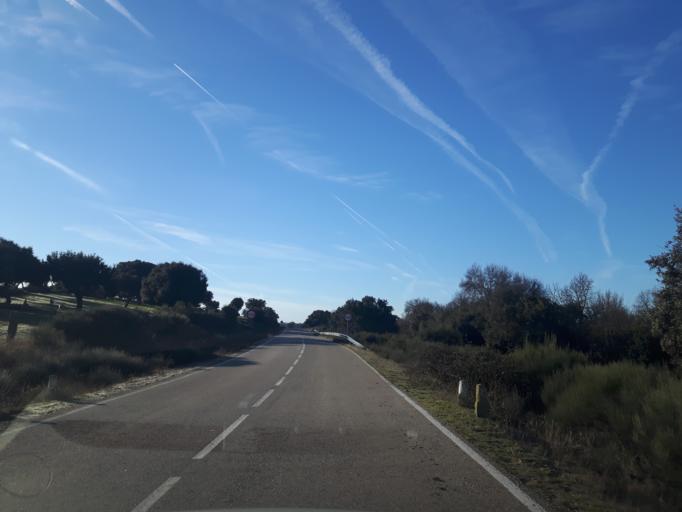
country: ES
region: Castille and Leon
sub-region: Provincia de Salamanca
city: Olmedo de Camaces
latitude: 40.8902
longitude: -6.6229
